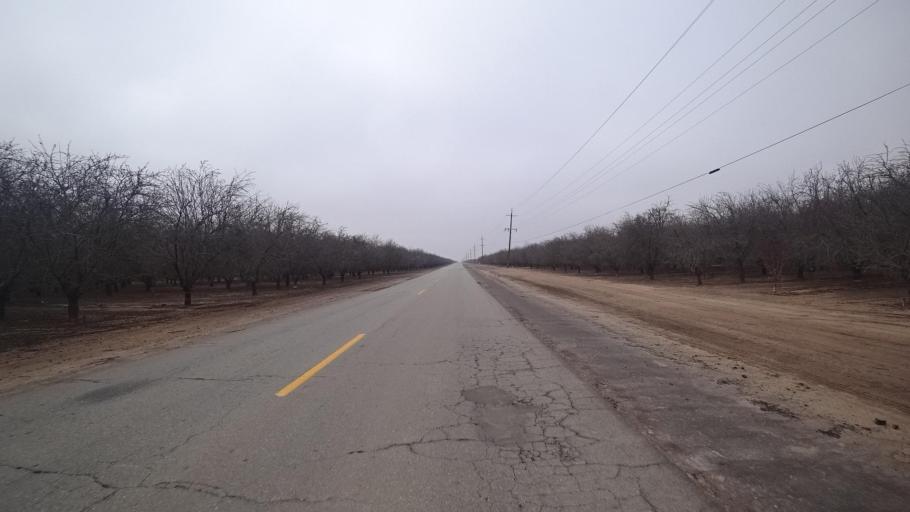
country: US
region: California
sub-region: Kern County
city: Maricopa
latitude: 35.0938
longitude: -119.2799
